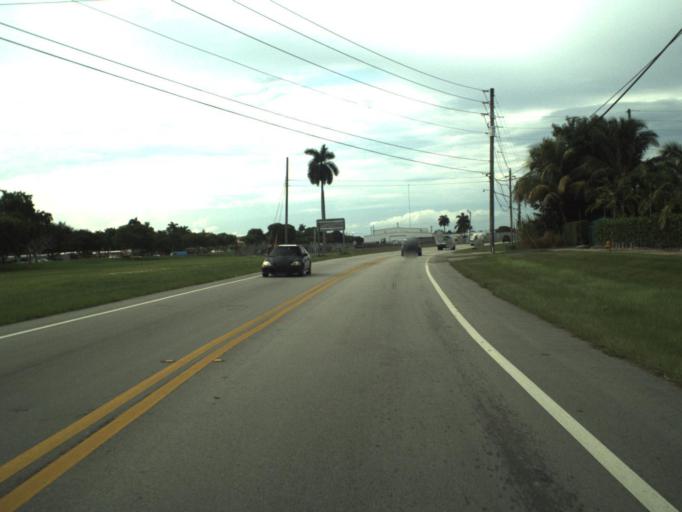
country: US
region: Florida
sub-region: Miami-Dade County
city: Florida City
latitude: 25.4397
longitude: -80.4768
